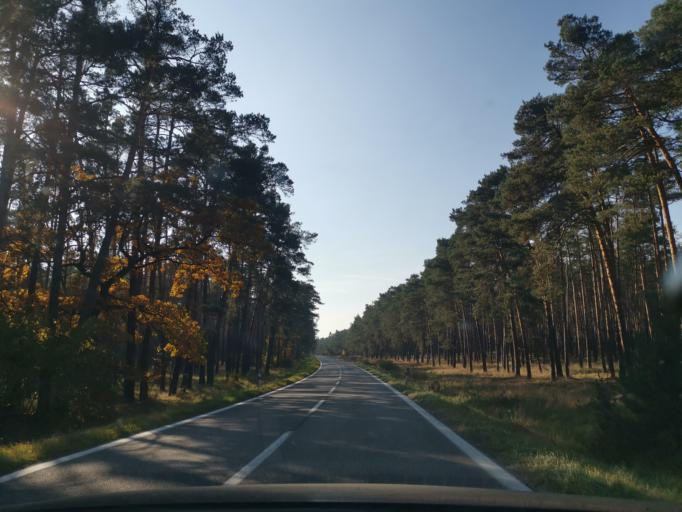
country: SK
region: Bratislavsky
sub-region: Okres Malacky
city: Malacky
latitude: 48.5036
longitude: 17.1119
